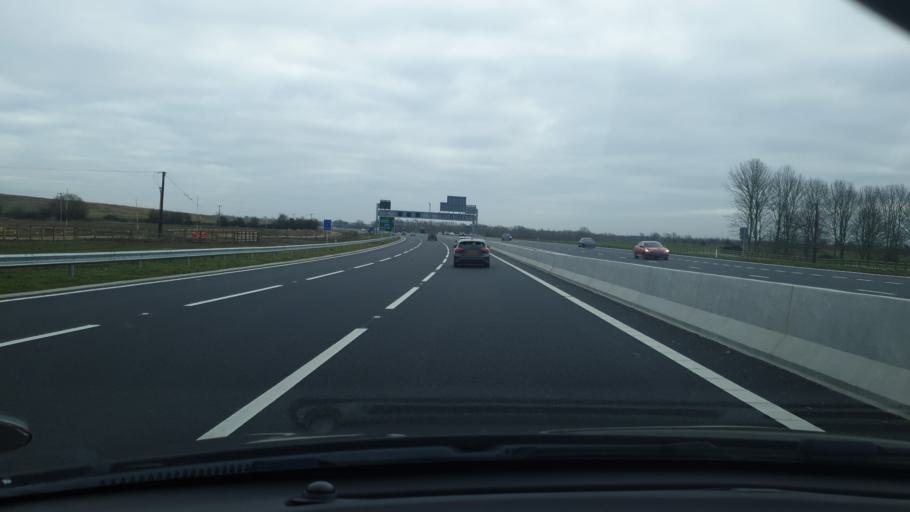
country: GB
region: England
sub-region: Cambridgeshire
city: Buckden
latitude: 52.3031
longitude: -0.2321
